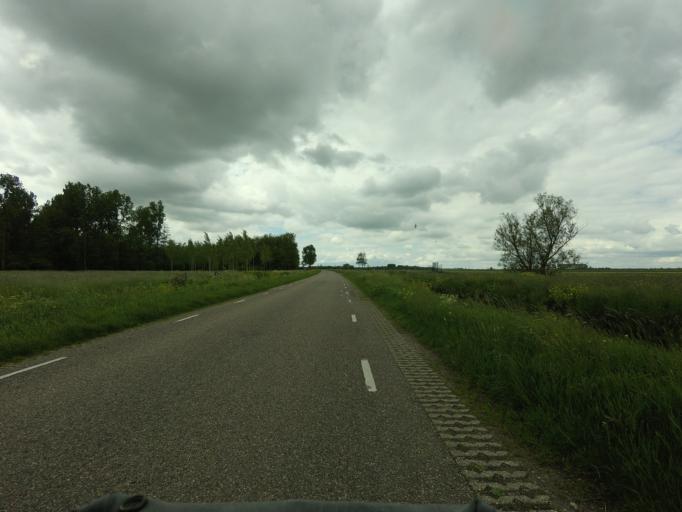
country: NL
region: Utrecht
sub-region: Gemeente Lopik
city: Lopik
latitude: 51.9326
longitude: 4.9334
